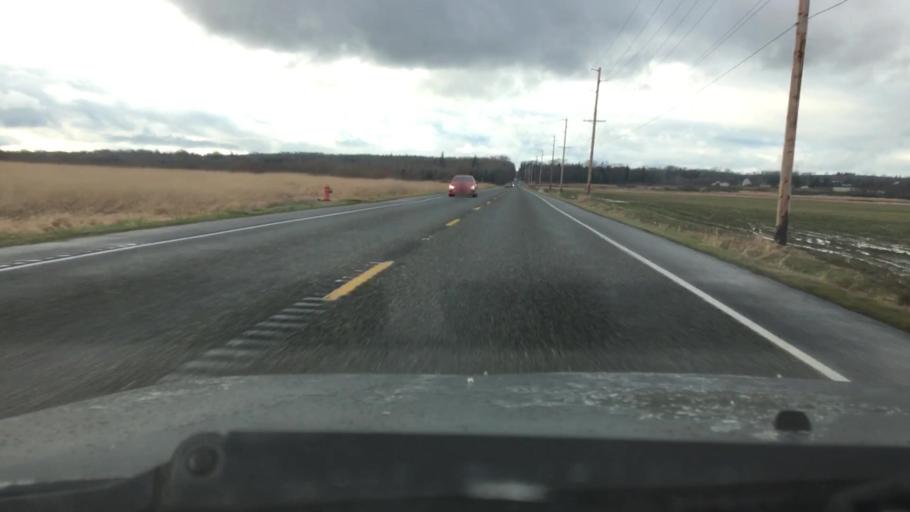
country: US
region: Washington
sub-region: Whatcom County
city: Ferndale
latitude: 48.8195
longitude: -122.6317
